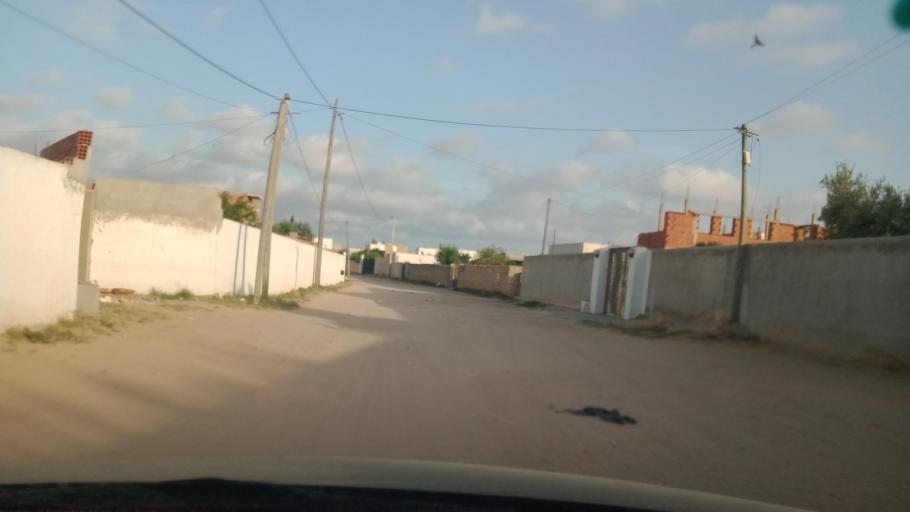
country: TN
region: Safaqis
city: Al Qarmadah
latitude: 34.8173
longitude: 10.7472
